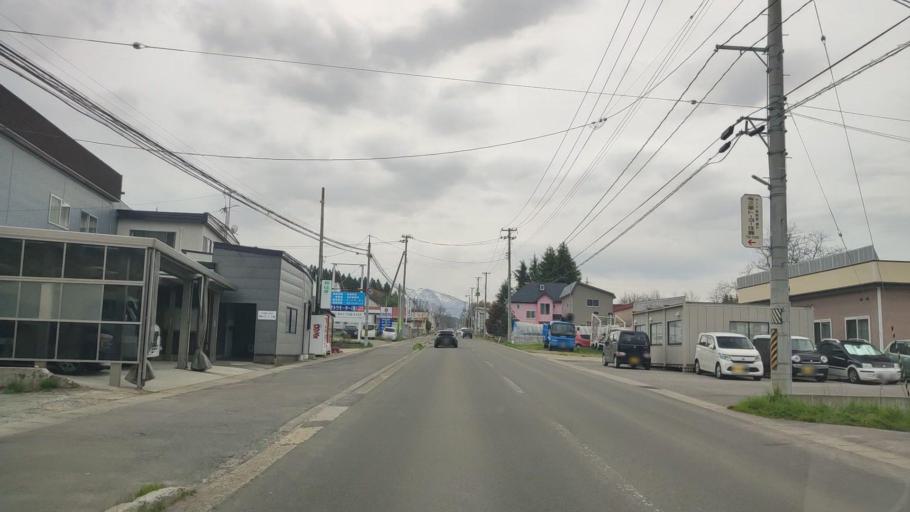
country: JP
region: Aomori
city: Aomori Shi
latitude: 40.7833
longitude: 140.7910
